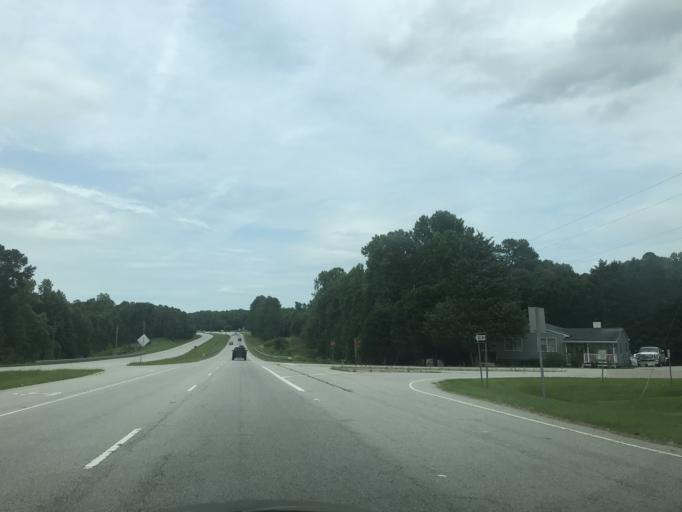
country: US
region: North Carolina
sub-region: Franklin County
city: Franklinton
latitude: 36.1111
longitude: -78.4588
